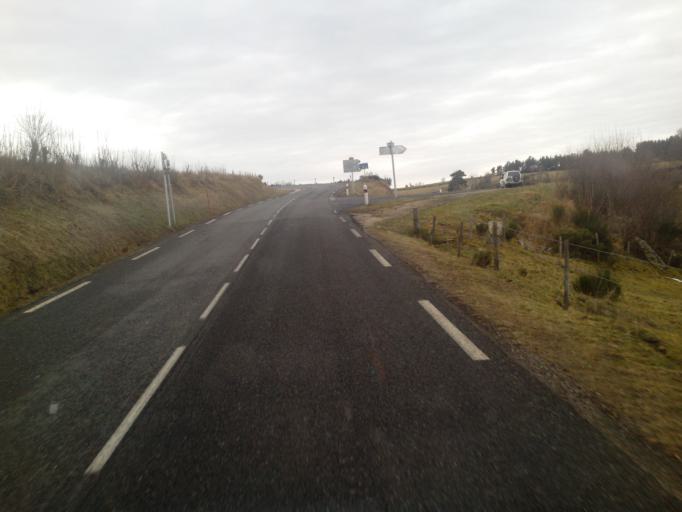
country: FR
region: Languedoc-Roussillon
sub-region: Departement de la Lozere
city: Mende
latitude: 44.6252
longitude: 3.4749
